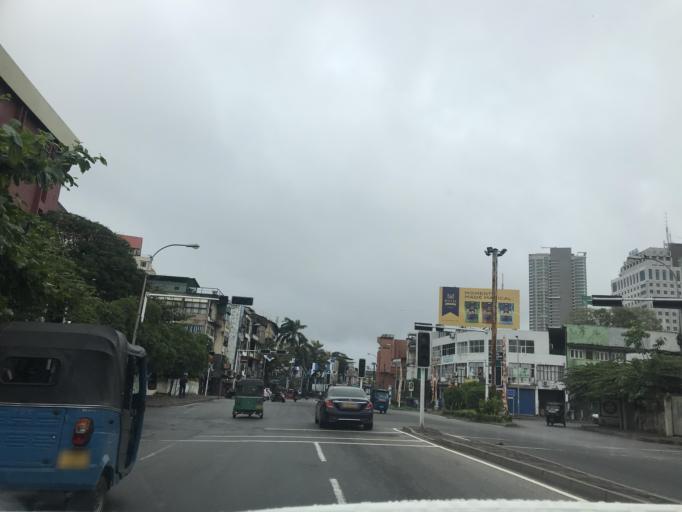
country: LK
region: Western
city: Colombo
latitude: 6.9236
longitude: 79.8648
